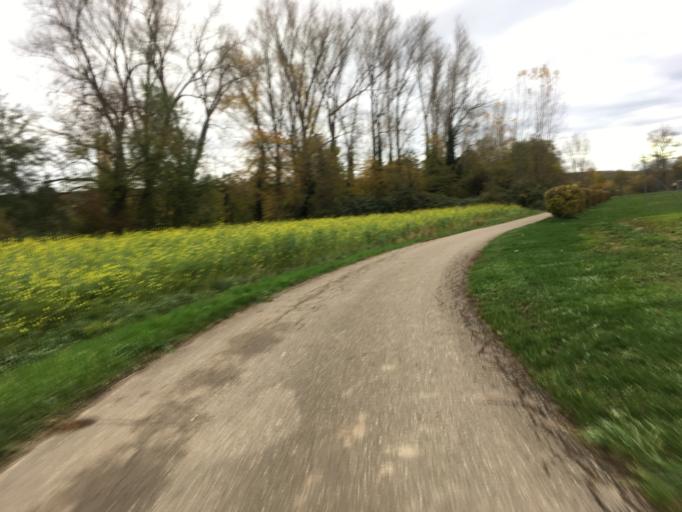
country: DE
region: Baden-Wuerttemberg
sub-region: Freiburg Region
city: Botzingen
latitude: 48.0726
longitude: 7.7281
